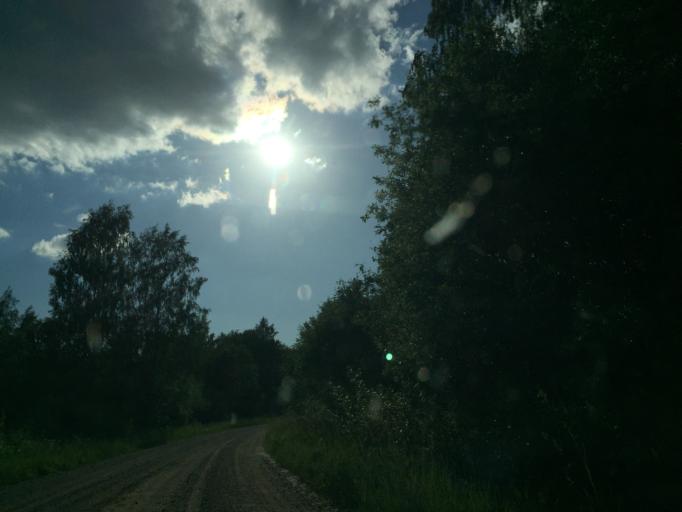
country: LV
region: Kandava
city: Kandava
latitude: 56.8379
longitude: 22.7596
